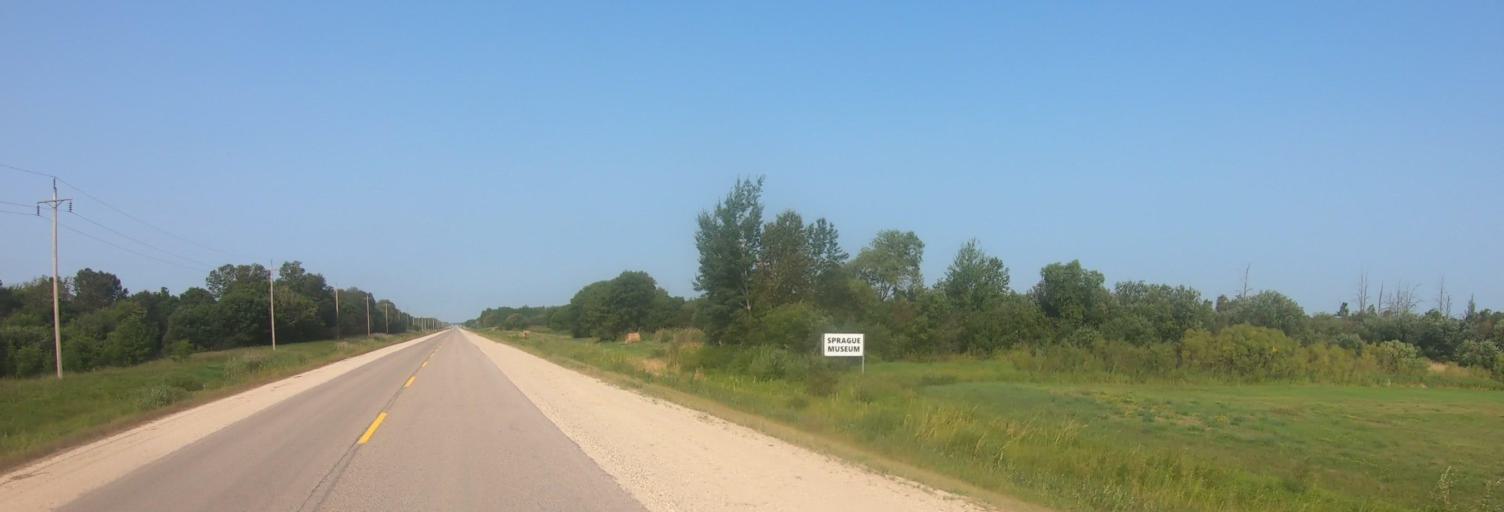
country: US
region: Minnesota
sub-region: Roseau County
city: Roseau
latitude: 49.0234
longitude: -95.6141
